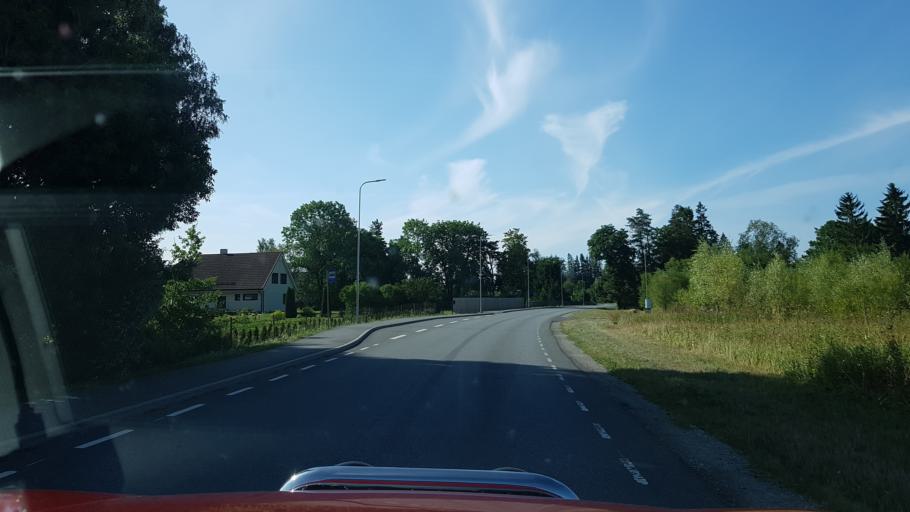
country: EE
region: Harju
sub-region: Joelaehtme vald
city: Loo
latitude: 59.3948
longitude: 24.9343
